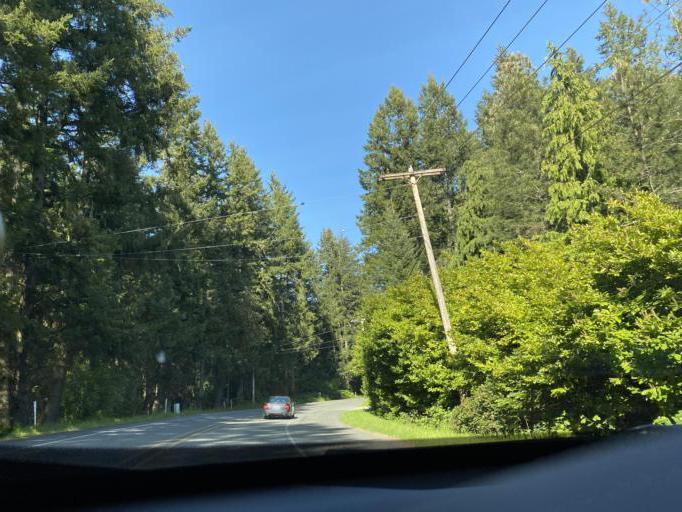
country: US
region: Washington
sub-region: Island County
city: Langley
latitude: 48.0324
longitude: -122.4453
